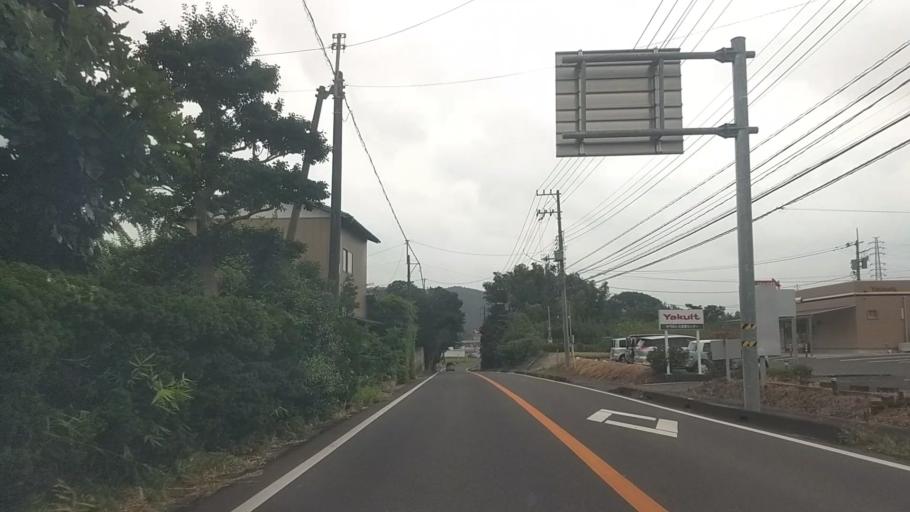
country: JP
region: Chiba
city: Kisarazu
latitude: 35.3116
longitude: 140.0632
